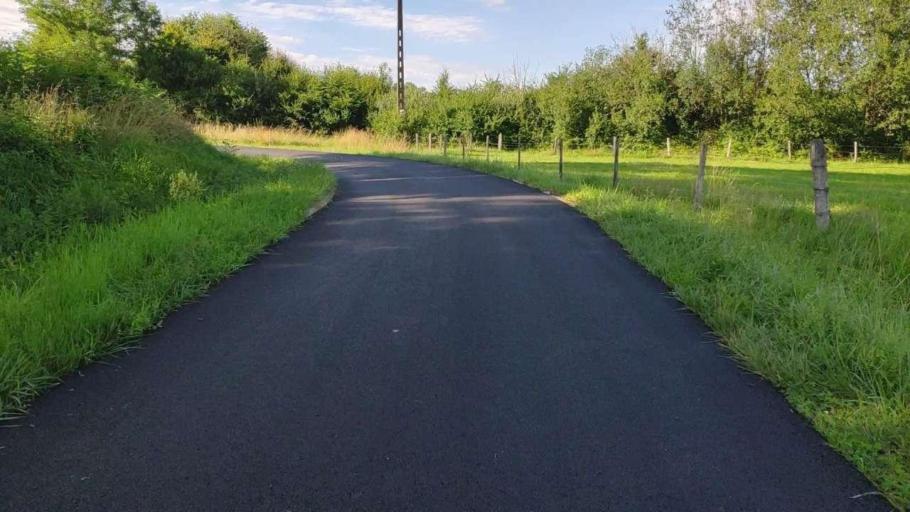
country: FR
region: Franche-Comte
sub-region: Departement du Jura
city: Bletterans
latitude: 46.8288
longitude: 5.5015
